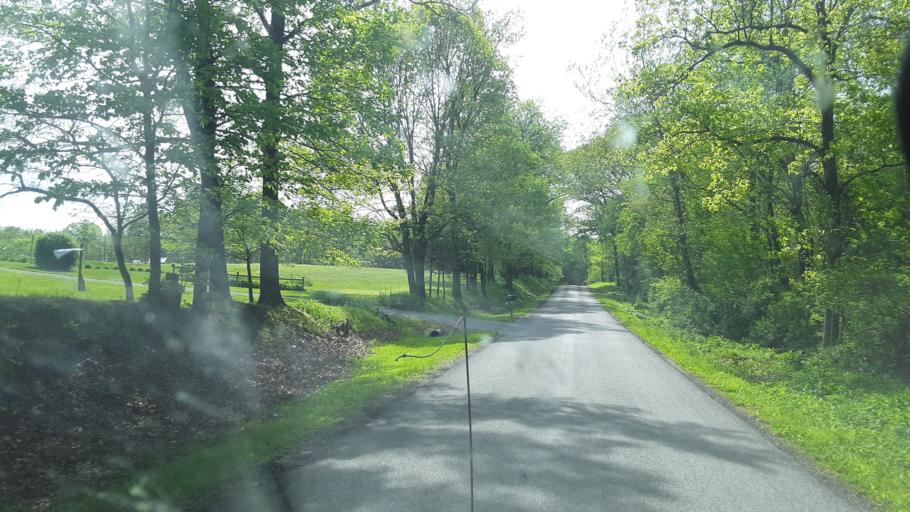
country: US
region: Illinois
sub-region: Jackson County
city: Carbondale
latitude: 37.6800
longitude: -89.2659
